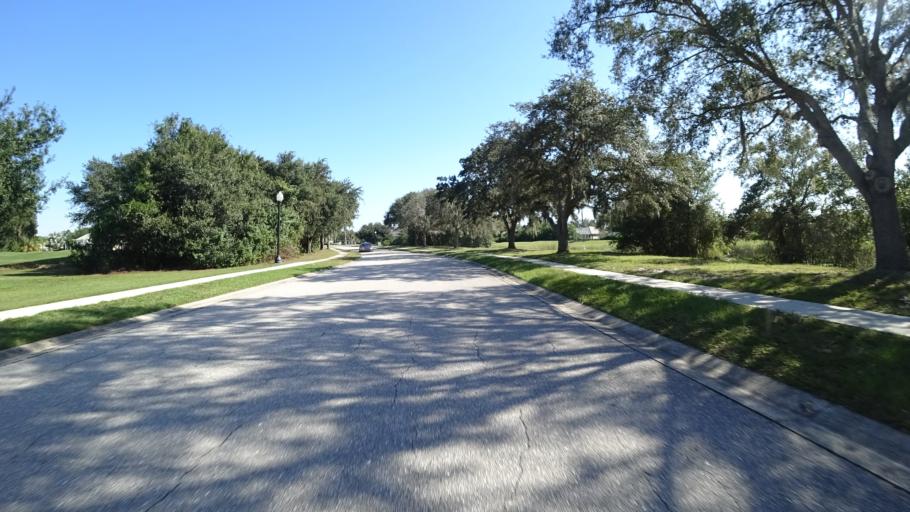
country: US
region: Florida
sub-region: Sarasota County
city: The Meadows
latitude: 27.4158
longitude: -82.4387
